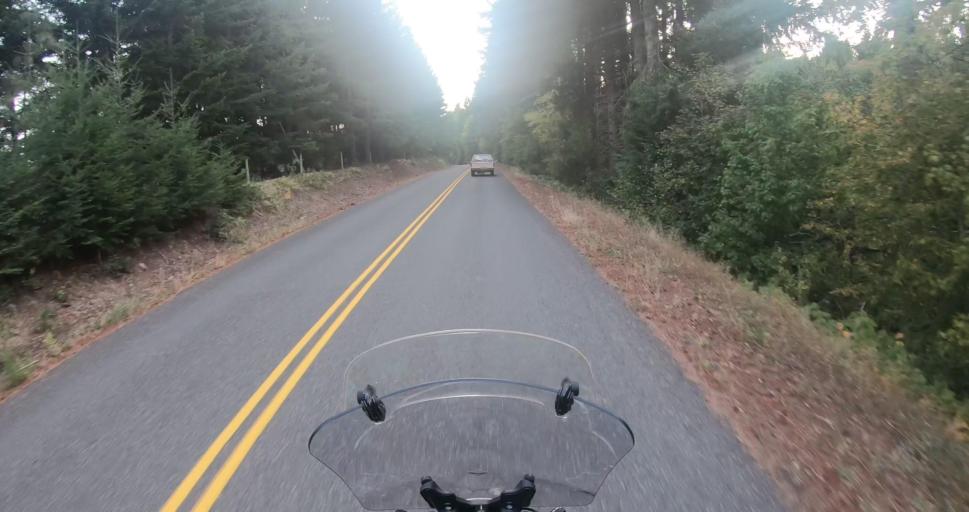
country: US
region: Oregon
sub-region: Hood River County
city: Odell
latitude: 45.4772
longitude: -121.6030
